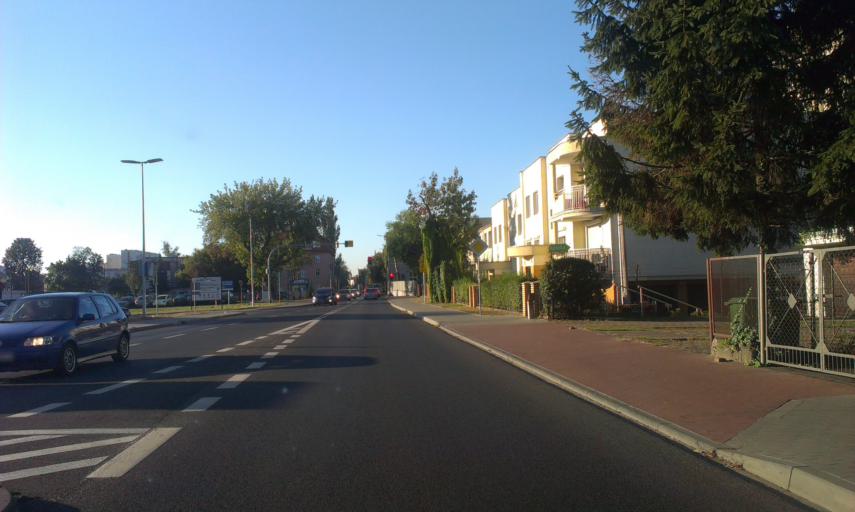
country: PL
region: Kujawsko-Pomorskie
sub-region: Torun
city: Torun
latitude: 53.0259
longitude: 18.6015
